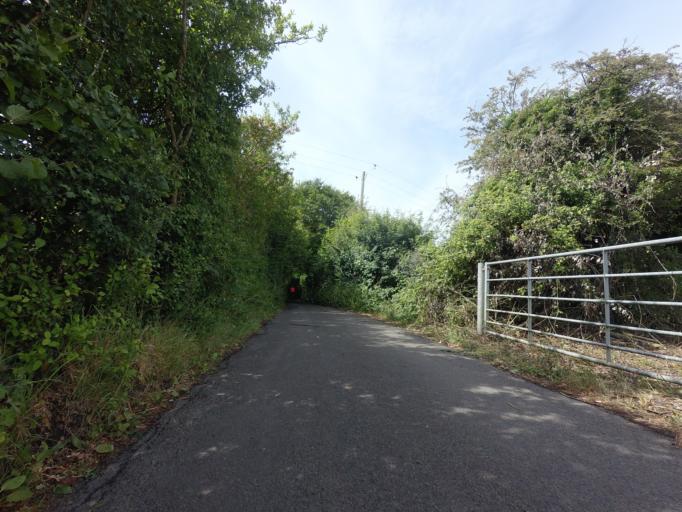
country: GB
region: England
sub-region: Greater London
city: Orpington
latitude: 51.3692
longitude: 0.1315
